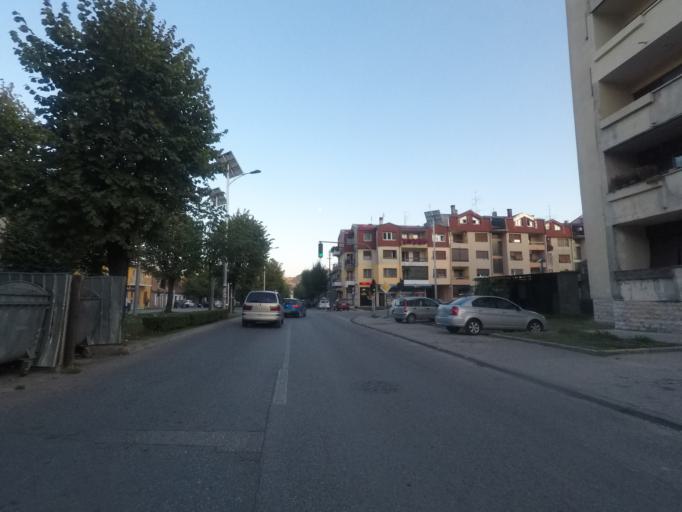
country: ME
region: Cetinje
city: Cetinje
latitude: 42.3936
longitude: 18.9180
